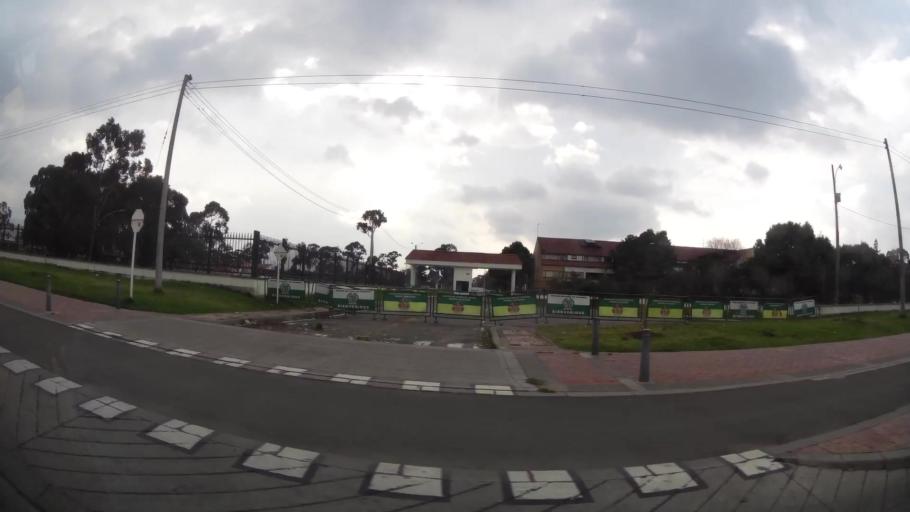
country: CO
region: Bogota D.C.
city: Bogota
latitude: 4.5897
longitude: -74.1284
